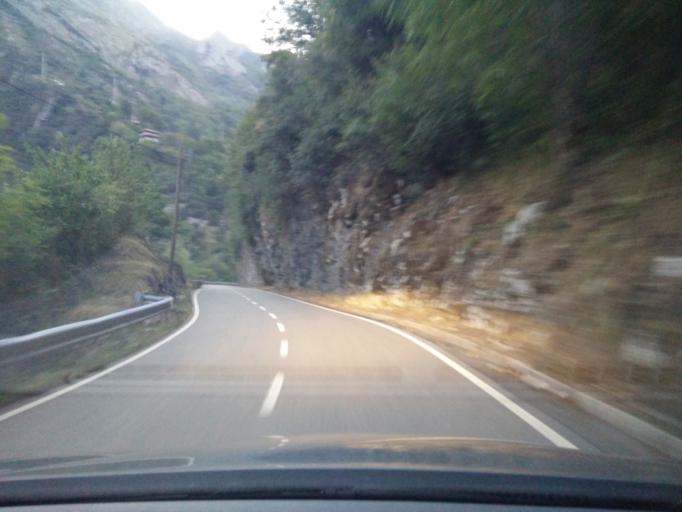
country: ES
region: Asturias
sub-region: Province of Asturias
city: Amieva
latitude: 43.2112
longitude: -5.0920
